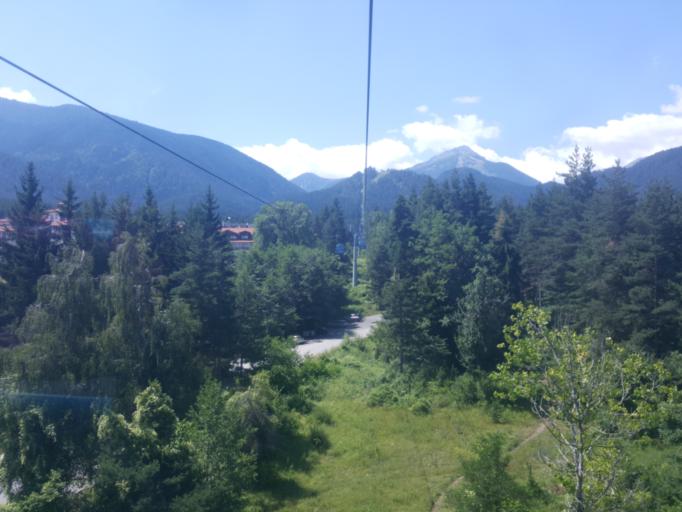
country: BG
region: Blagoevgrad
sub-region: Obshtina Bansko
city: Bansko
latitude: 41.8220
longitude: 23.4753
